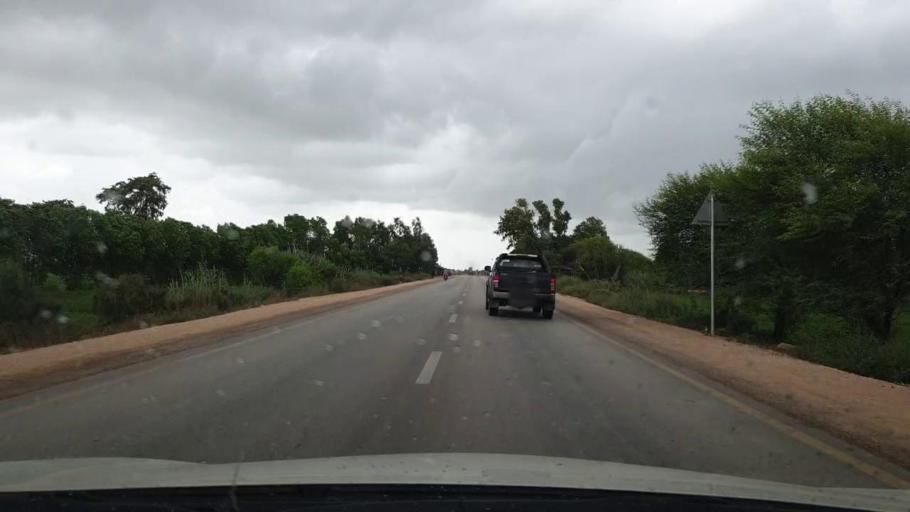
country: PK
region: Sindh
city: Kario
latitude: 24.6427
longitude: 68.4668
